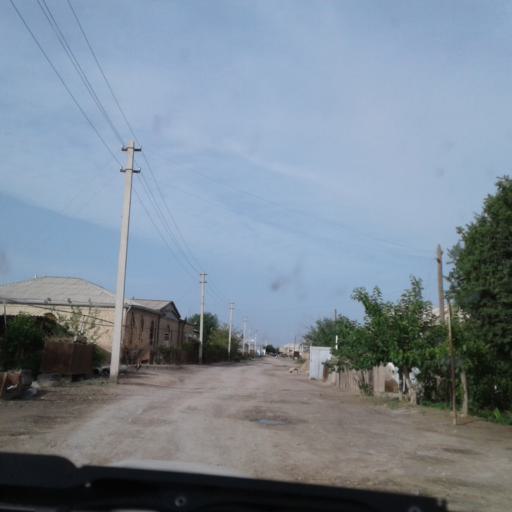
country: TM
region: Mary
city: Mary
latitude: 37.5801
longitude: 61.8729
